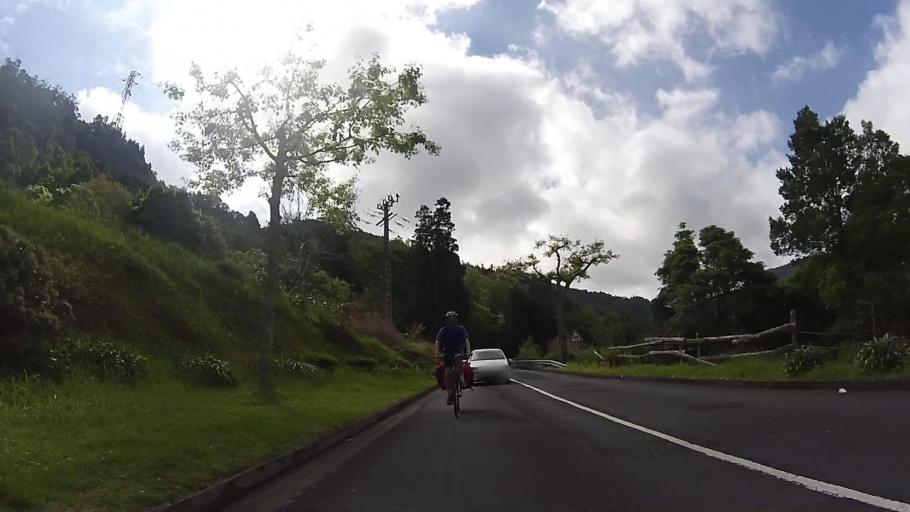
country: PT
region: Azores
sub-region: Povoacao
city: Furnas
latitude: 37.7681
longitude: -25.2903
